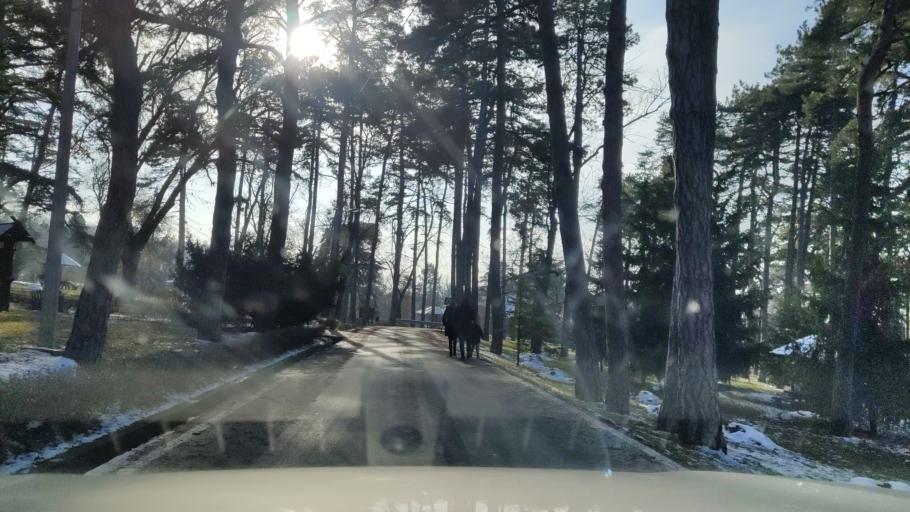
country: RS
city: Rusanj
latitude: 44.6962
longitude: 20.5046
